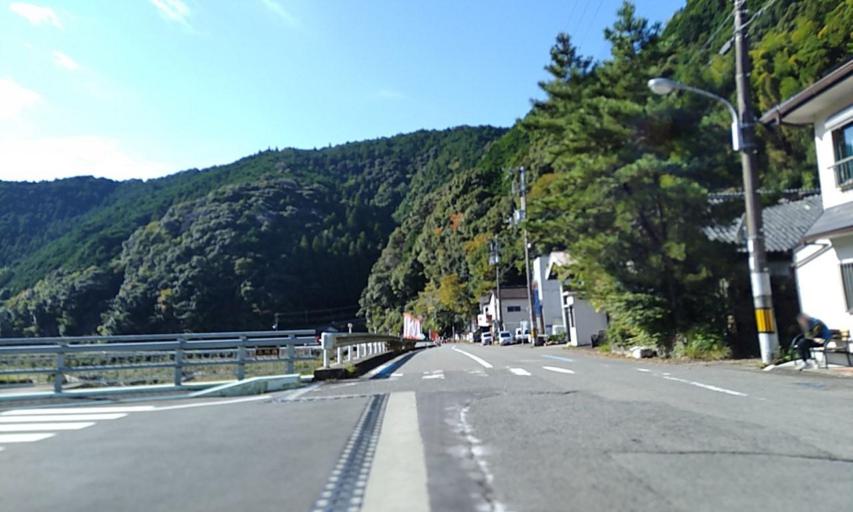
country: JP
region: Wakayama
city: Kainan
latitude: 34.0710
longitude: 135.3559
